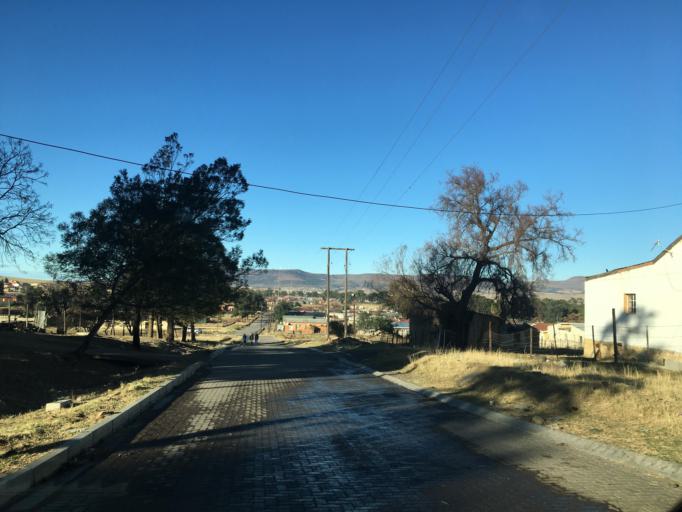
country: ZA
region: Eastern Cape
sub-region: Chris Hani District Municipality
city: Cala
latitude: -31.5269
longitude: 27.6965
